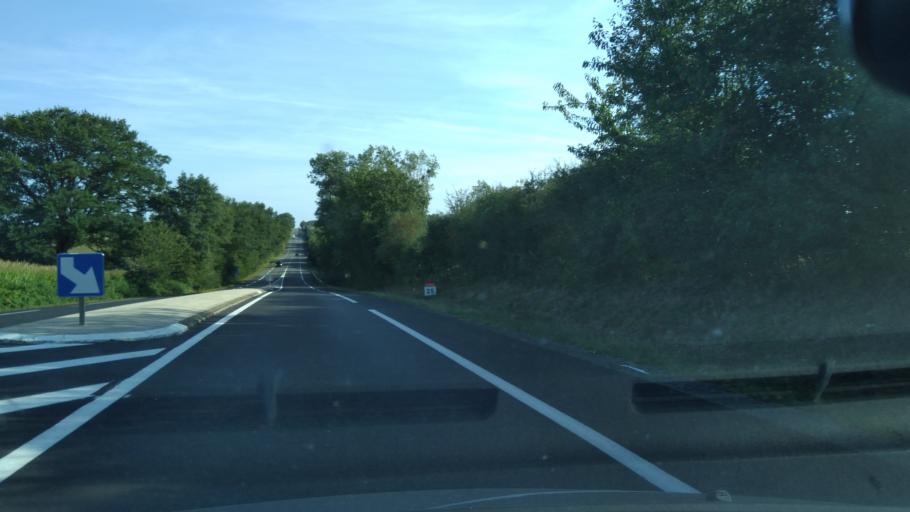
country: FR
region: Pays de la Loire
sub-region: Departement de la Mayenne
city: Entrammes
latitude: 47.9625
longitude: -0.7043
